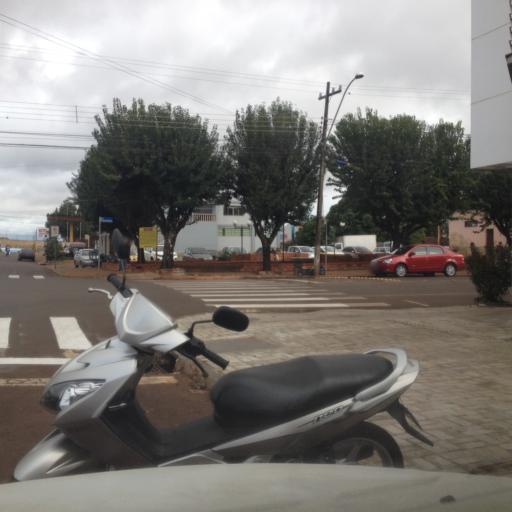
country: BR
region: Parana
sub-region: Matelandia
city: Matelandia
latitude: -25.2414
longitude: -53.9757
